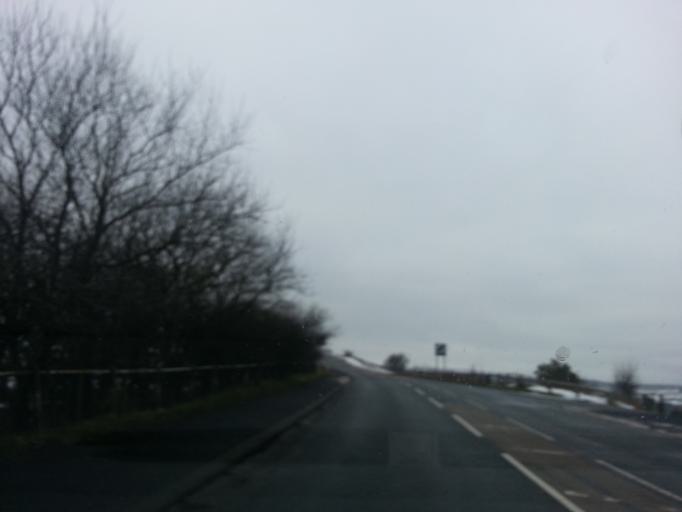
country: GB
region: England
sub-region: County Durham
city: Tow Law
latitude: 54.7412
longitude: -1.7874
